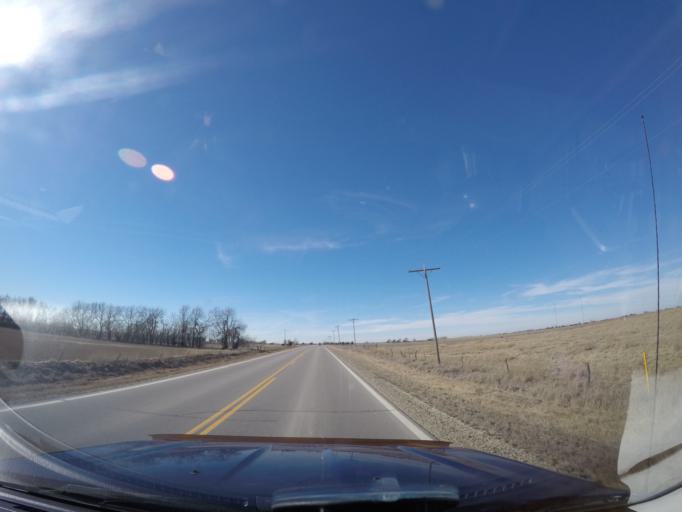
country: US
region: Kansas
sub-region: Dickinson County
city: Herington
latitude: 38.6674
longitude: -96.9021
